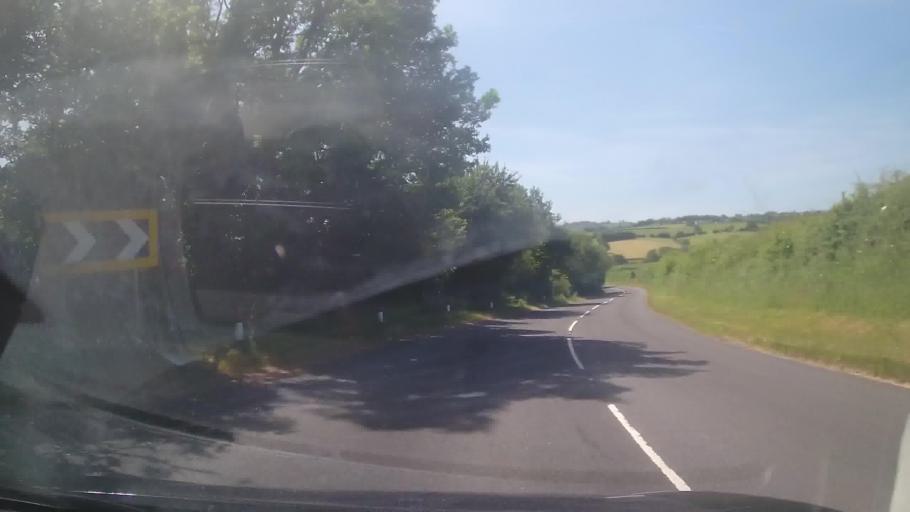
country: GB
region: England
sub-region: Herefordshire
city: Pencoyd
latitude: 51.9027
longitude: -2.7294
